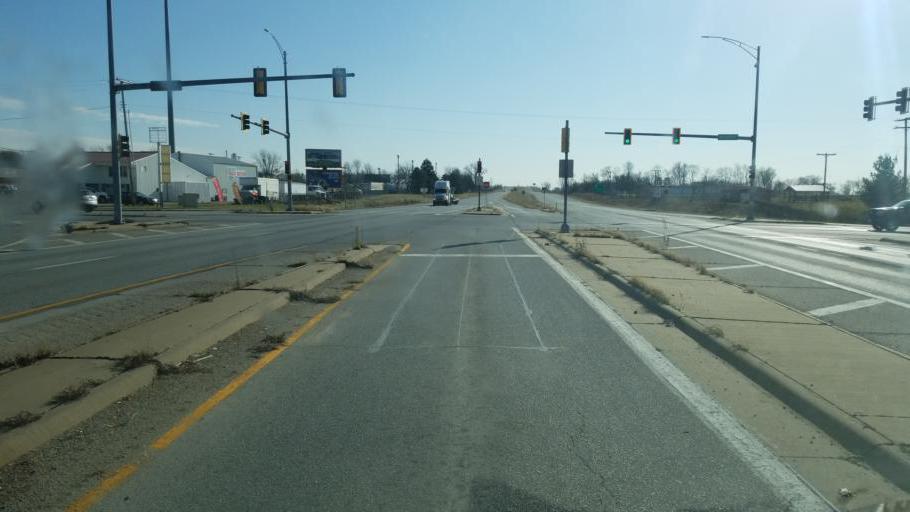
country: US
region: Illinois
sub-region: Warren County
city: Monmouth
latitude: 40.9128
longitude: -90.6631
